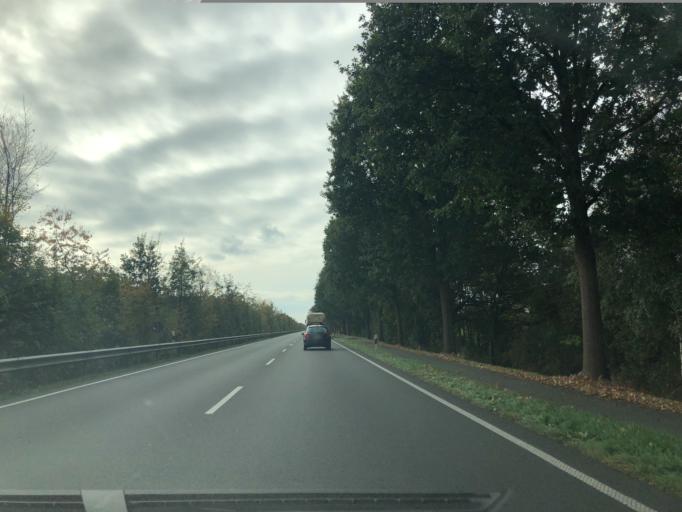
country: DE
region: Lower Saxony
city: Friesoythe
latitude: 53.0533
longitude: 7.8002
